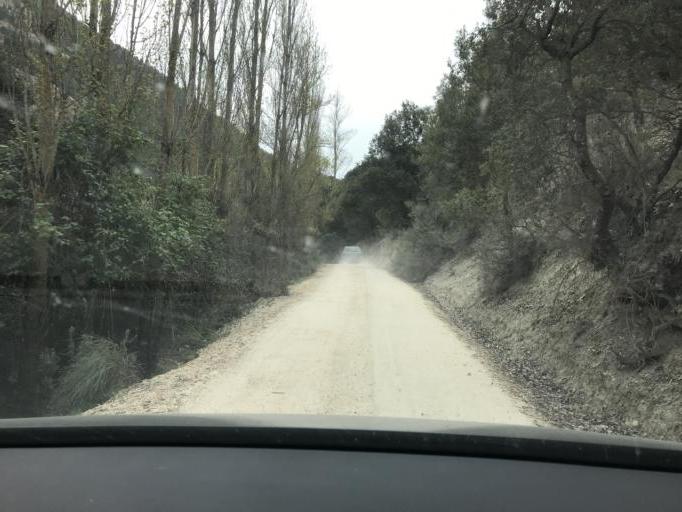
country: ES
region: Andalusia
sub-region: Provincia de Granada
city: Castril
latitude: 37.8688
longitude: -2.7623
